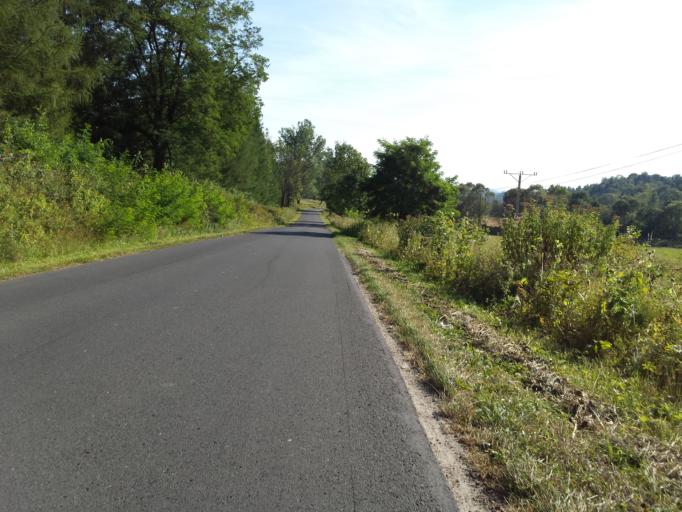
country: PL
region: Subcarpathian Voivodeship
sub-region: Powiat leski
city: Olszanica
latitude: 49.5002
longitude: 22.4508
